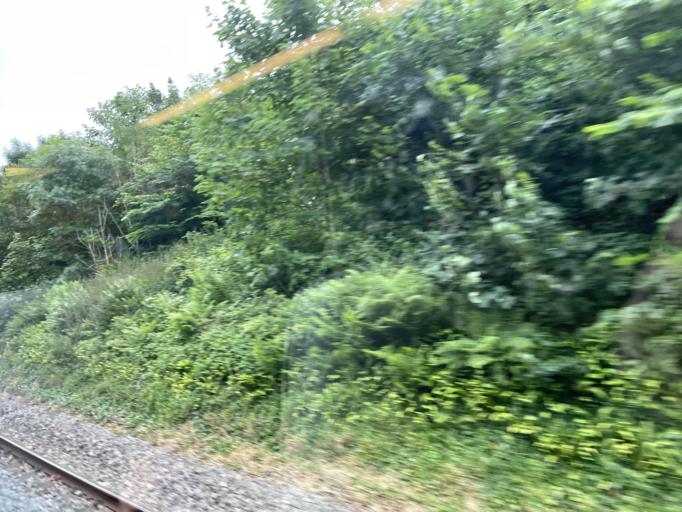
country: GB
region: Wales
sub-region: Anglesey
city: Beaumaris
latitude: 53.2169
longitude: -4.0885
